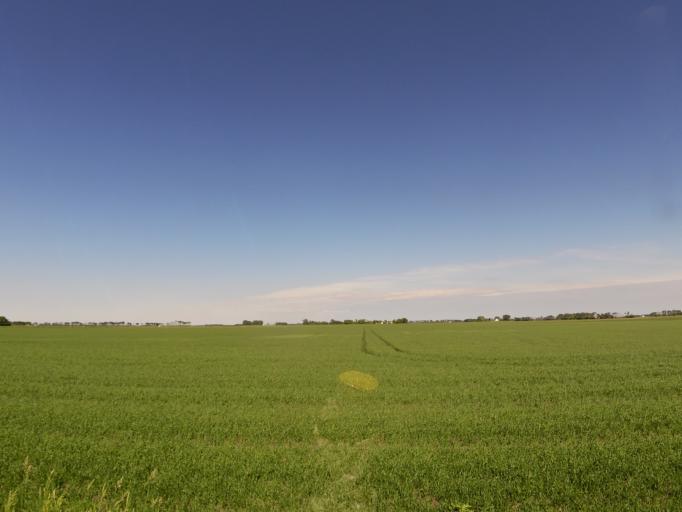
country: US
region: North Dakota
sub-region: Walsh County
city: Grafton
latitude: 48.3508
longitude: -97.2558
